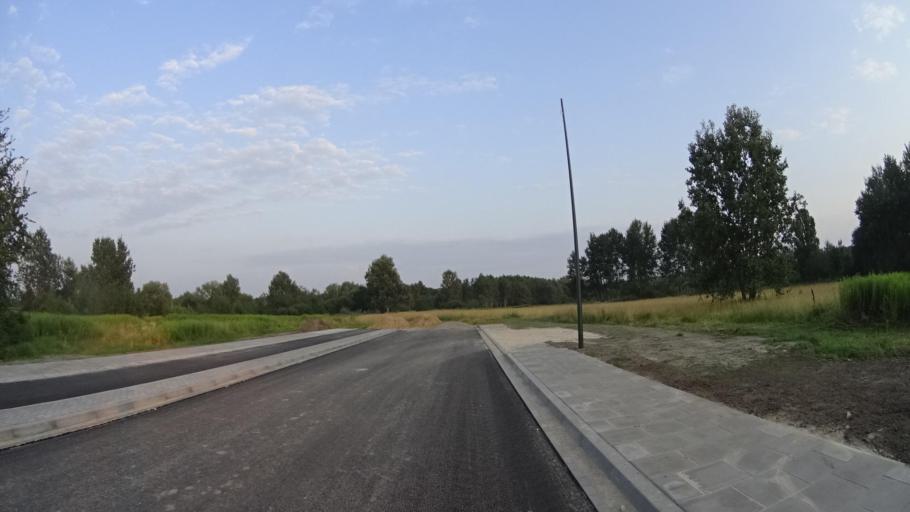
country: PL
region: Masovian Voivodeship
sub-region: Warszawa
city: Wilanow
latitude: 52.1518
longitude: 21.0726
